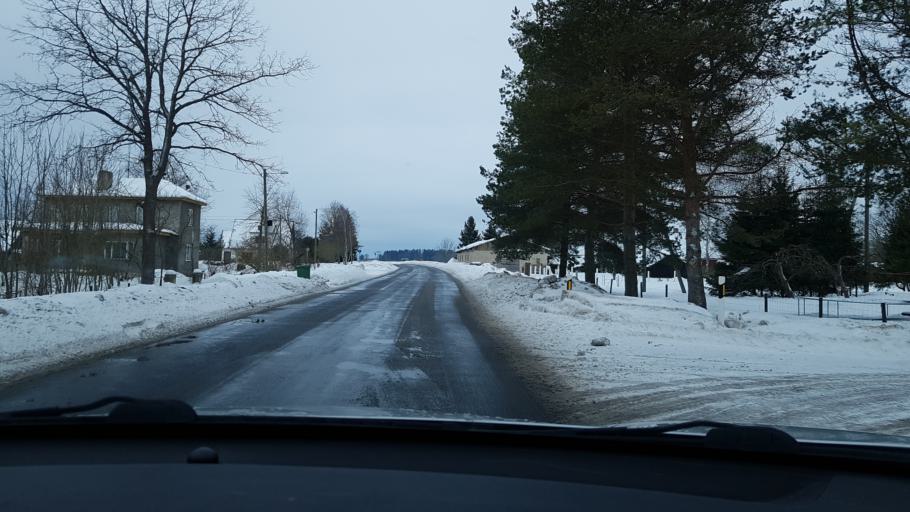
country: EE
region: Jaervamaa
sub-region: Jaerva-Jaani vald
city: Jarva-Jaani
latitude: 59.1492
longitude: 25.7523
